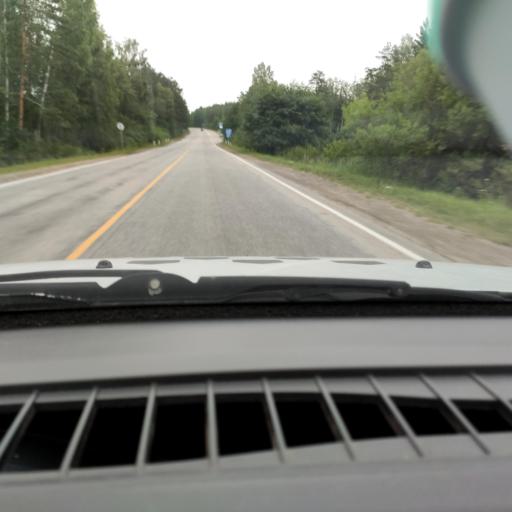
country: RU
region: Chelyabinsk
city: Kyshtym
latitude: 55.7332
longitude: 60.5303
